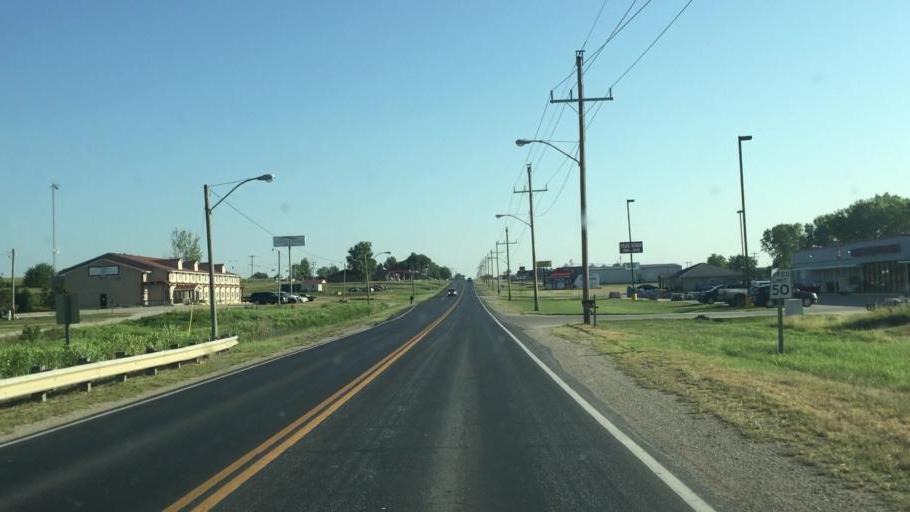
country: US
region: Kansas
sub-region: Nemaha County
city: Sabetha
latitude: 39.8891
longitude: -95.7883
